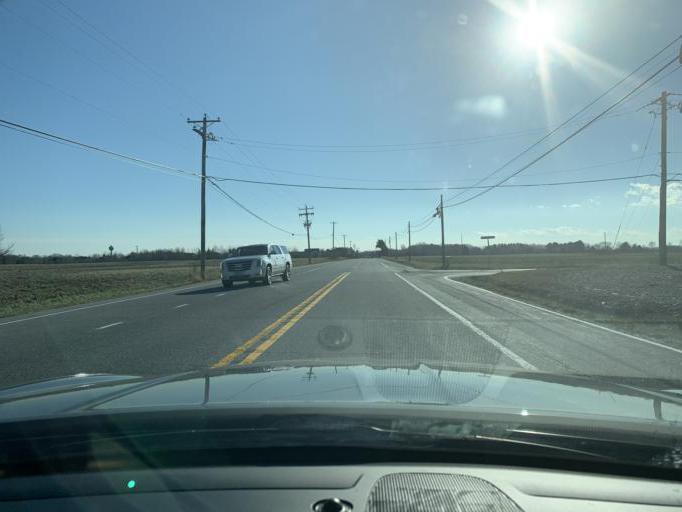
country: US
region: Maryland
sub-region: Queen Anne's County
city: Centreville
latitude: 39.0685
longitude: -76.0495
